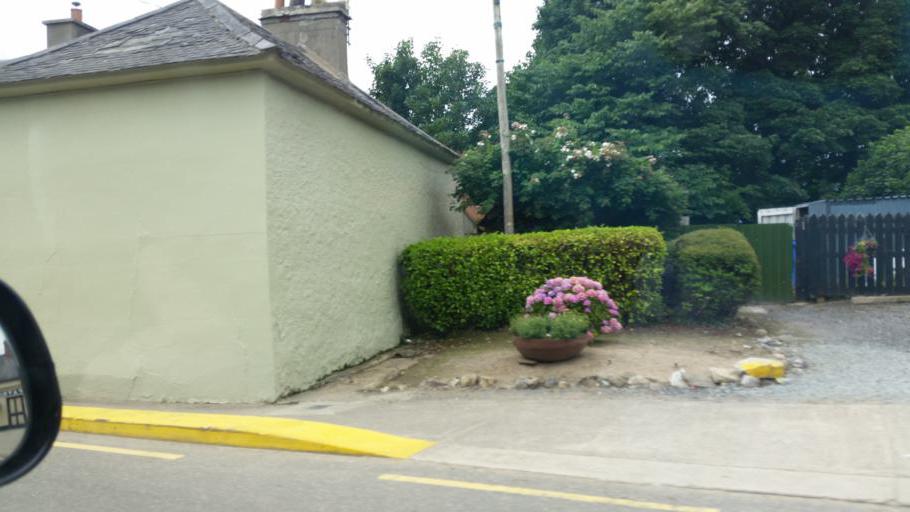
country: IE
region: Leinster
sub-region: Loch Garman
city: Castlebridge
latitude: 52.4122
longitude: -6.4089
